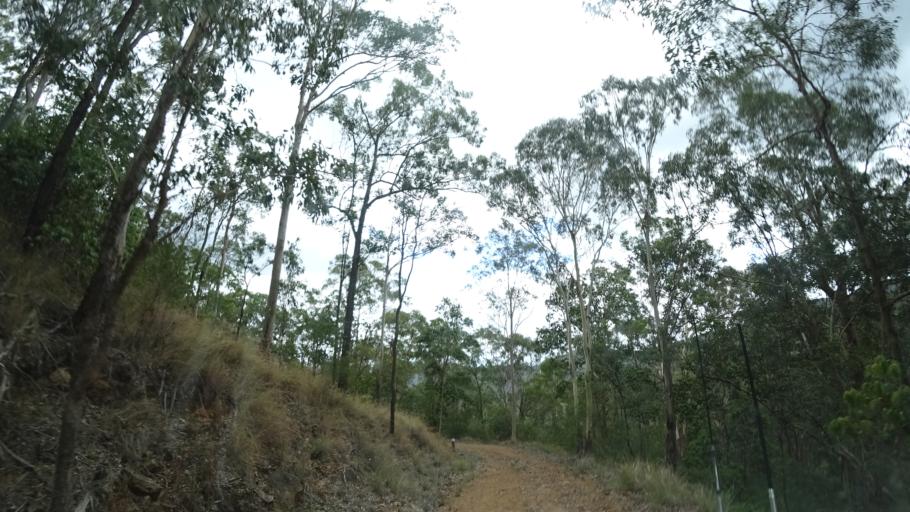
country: AU
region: Queensland
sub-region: Moreton Bay
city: Highvale
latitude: -27.4233
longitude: 152.7736
